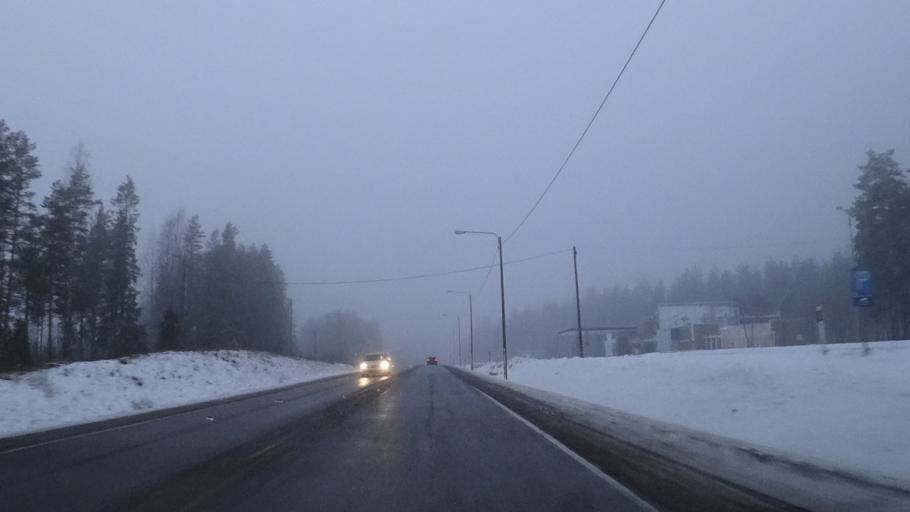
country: FI
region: Paijanne Tavastia
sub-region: Lahti
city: Hollola
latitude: 60.9885
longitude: 25.3932
